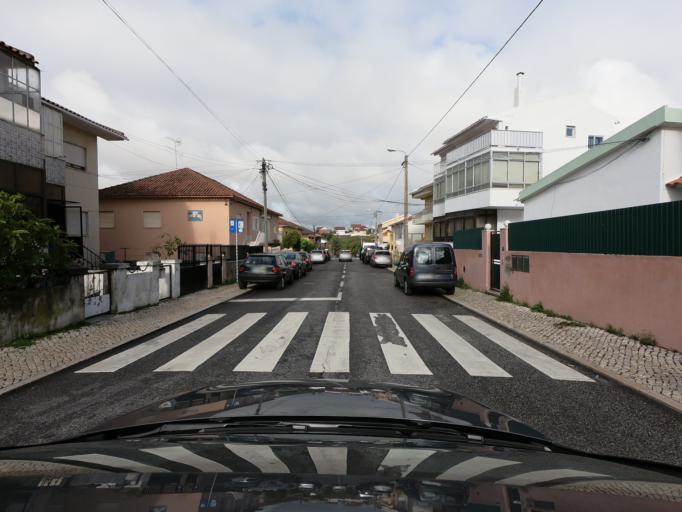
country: PT
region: Lisbon
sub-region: Oeiras
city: Porto Salvo
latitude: 38.7226
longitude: -9.3078
